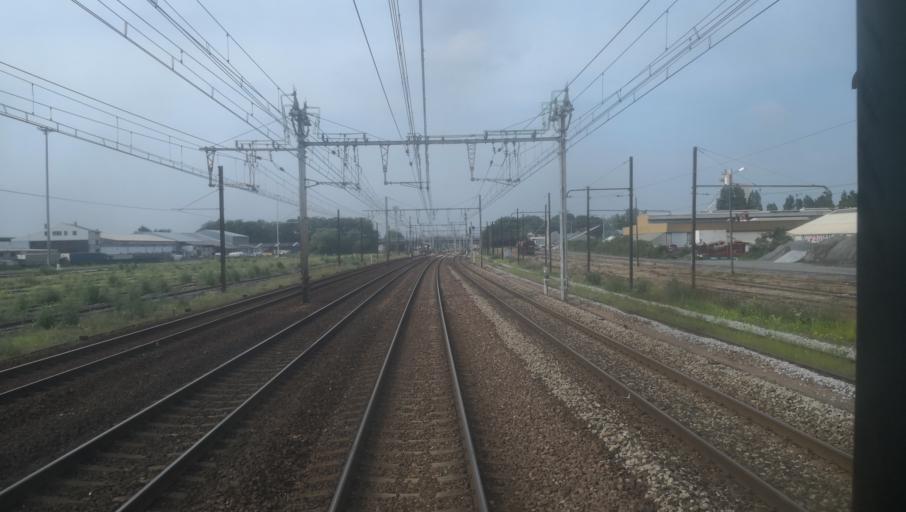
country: FR
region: Ile-de-France
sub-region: Departement de l'Essonne
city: Marolles-en-Hurepoix
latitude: 48.5828
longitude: 2.2905
